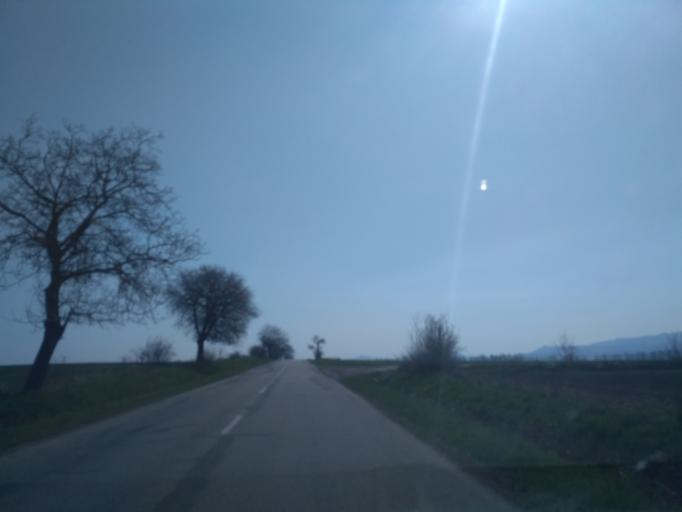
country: SK
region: Kosicky
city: Secovce
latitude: 48.6781
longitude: 21.6154
